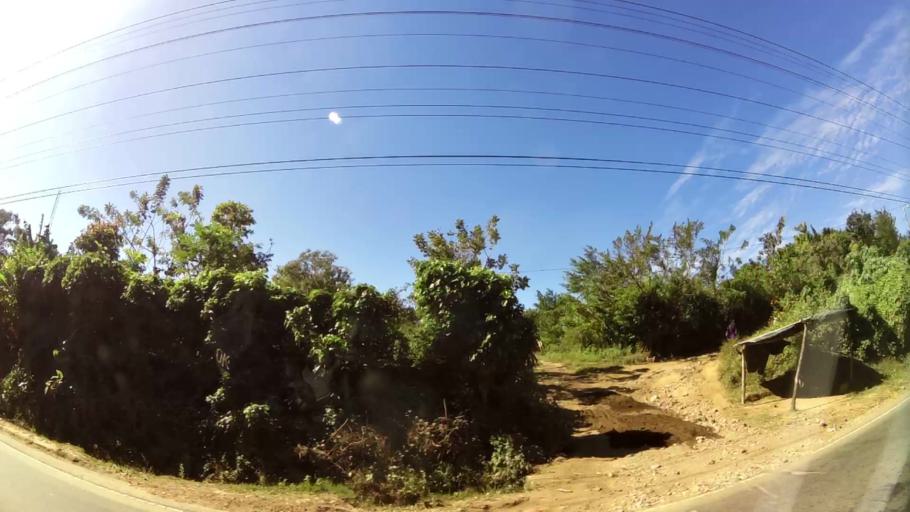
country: SV
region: Sonsonate
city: Juayua
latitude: 13.8344
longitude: -89.7621
